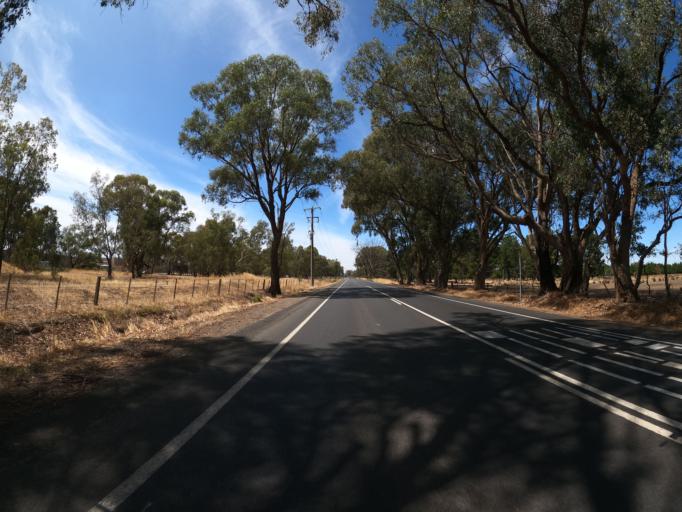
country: AU
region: Victoria
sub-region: Benalla
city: Benalla
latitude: -36.5246
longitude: 146.0376
